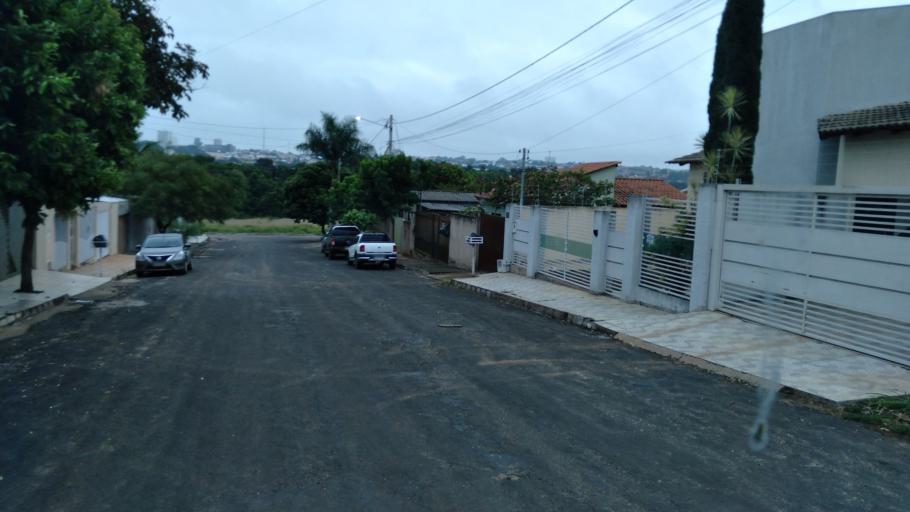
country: BR
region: Goias
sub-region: Mineiros
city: Mineiros
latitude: -17.5734
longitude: -52.5455
